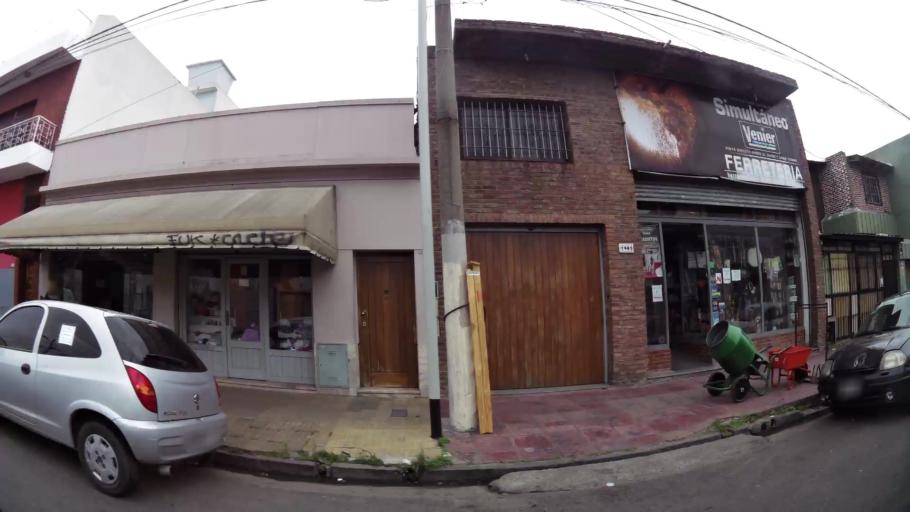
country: AR
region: Buenos Aires
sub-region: Partido de Avellaneda
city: Avellaneda
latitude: -34.6832
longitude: -58.3720
